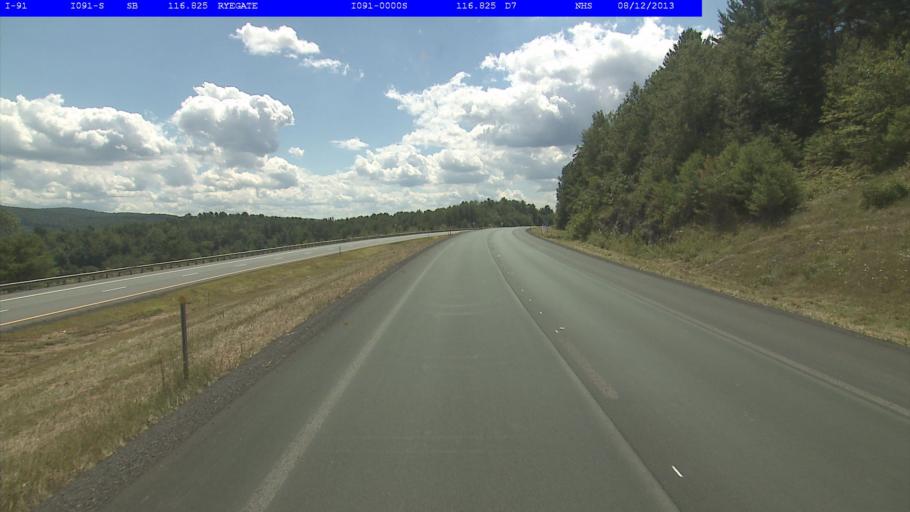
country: US
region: New Hampshire
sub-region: Grafton County
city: Woodsville
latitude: 44.2503
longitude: -72.0614
